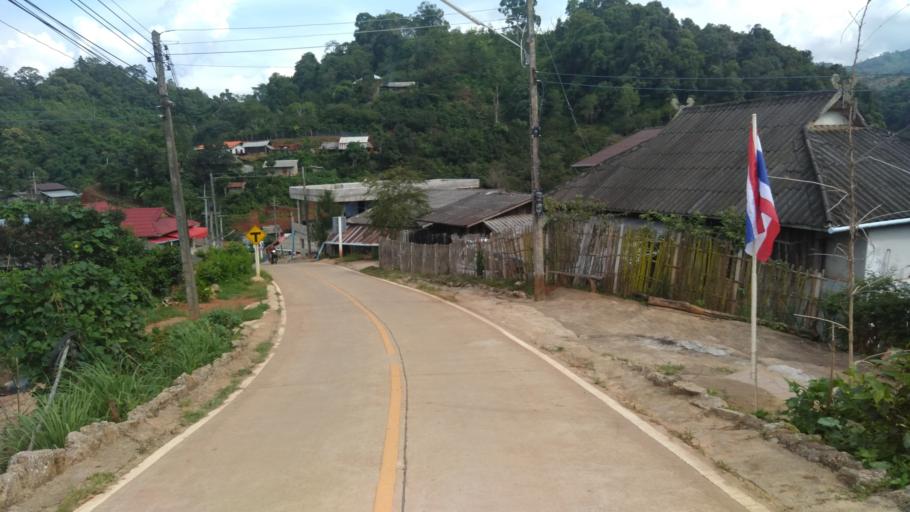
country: TH
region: Chiang Mai
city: Phrao
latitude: 19.5102
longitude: 99.3390
